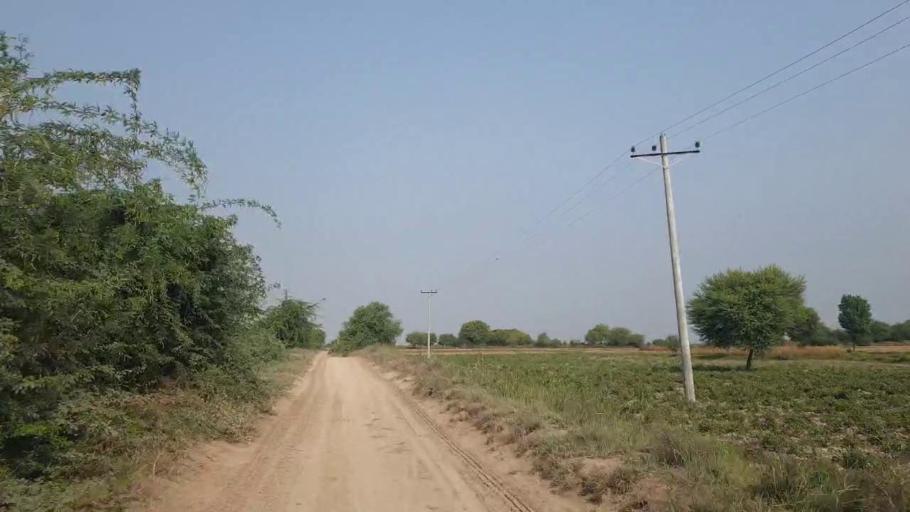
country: PK
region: Sindh
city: Badin
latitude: 24.6979
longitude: 68.7779
